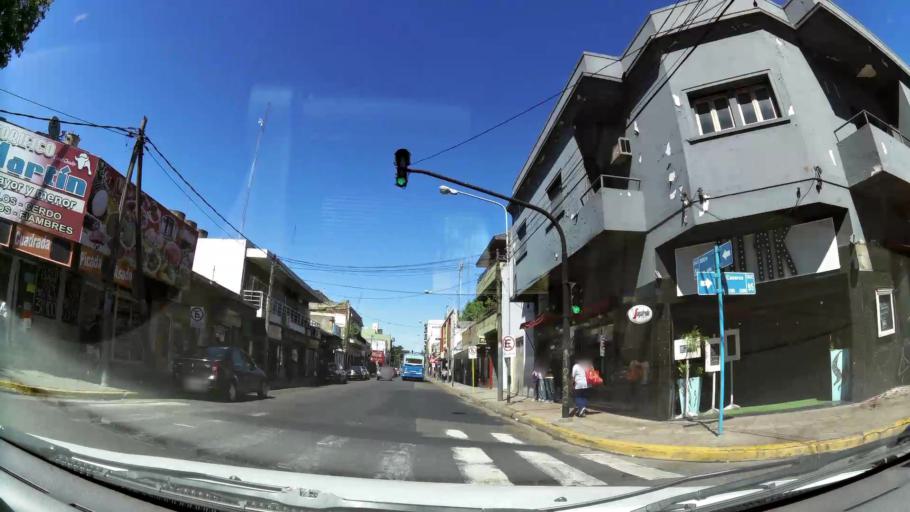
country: AR
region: Buenos Aires
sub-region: Partido de General San Martin
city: General San Martin
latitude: -34.5784
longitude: -58.5403
